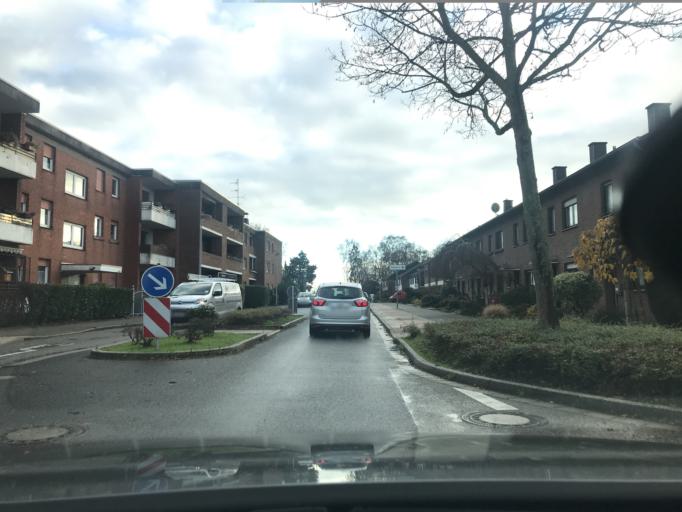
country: DE
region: North Rhine-Westphalia
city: Tonisvorst
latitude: 51.3716
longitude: 6.4986
